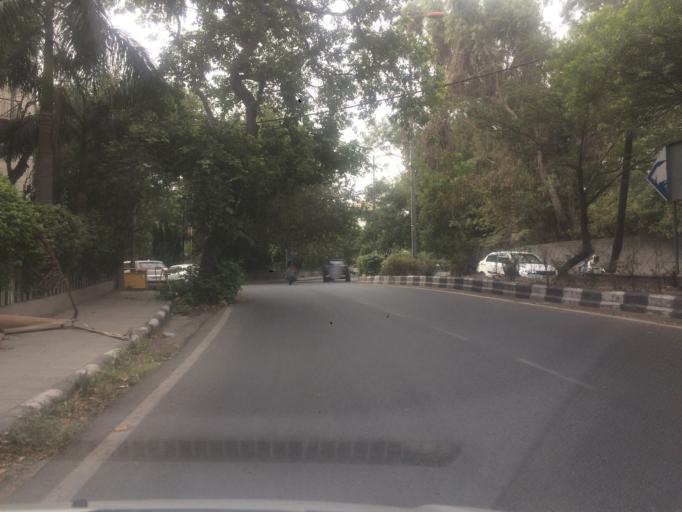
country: IN
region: NCT
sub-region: Central Delhi
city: Karol Bagh
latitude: 28.6319
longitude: 77.1750
